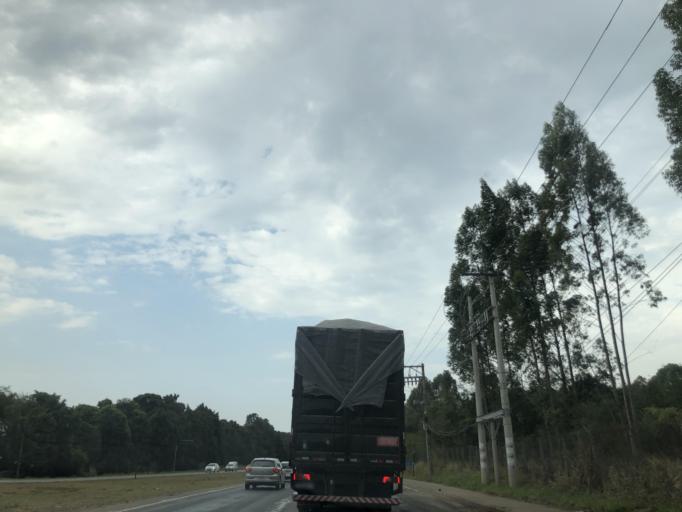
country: BR
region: Sao Paulo
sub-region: Salto De Pirapora
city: Salto de Pirapora
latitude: -23.5810
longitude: -47.5275
